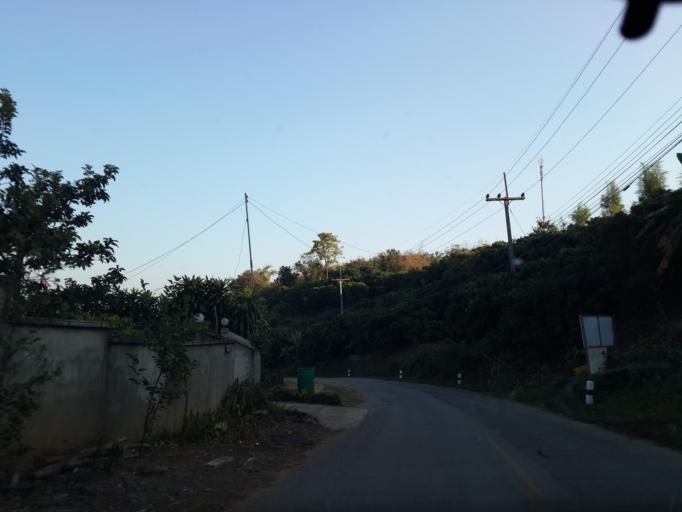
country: TH
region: Chiang Mai
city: Chai Prakan
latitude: 19.8176
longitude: 99.1007
